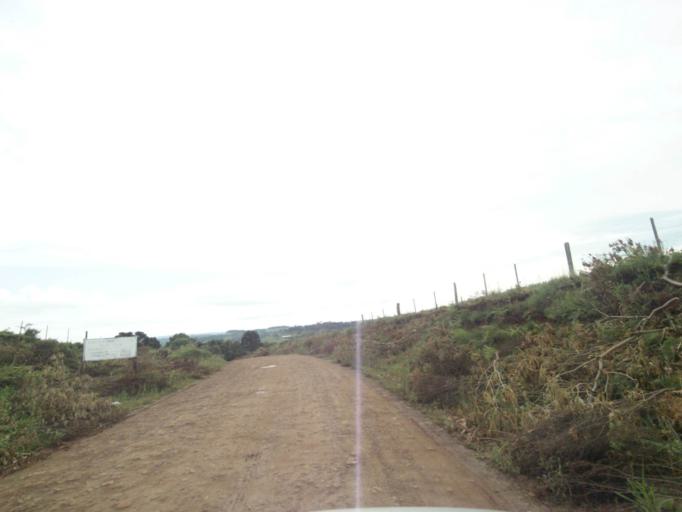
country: BR
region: Rio Grande do Sul
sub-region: Lagoa Vermelha
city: Lagoa Vermelha
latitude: -28.2386
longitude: -51.4963
